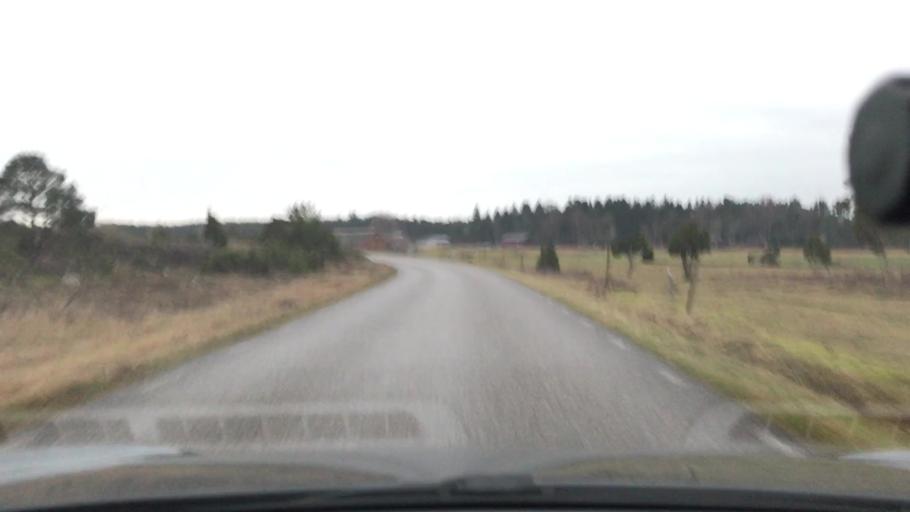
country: SE
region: Gotland
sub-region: Gotland
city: Slite
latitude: 57.3985
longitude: 18.8062
